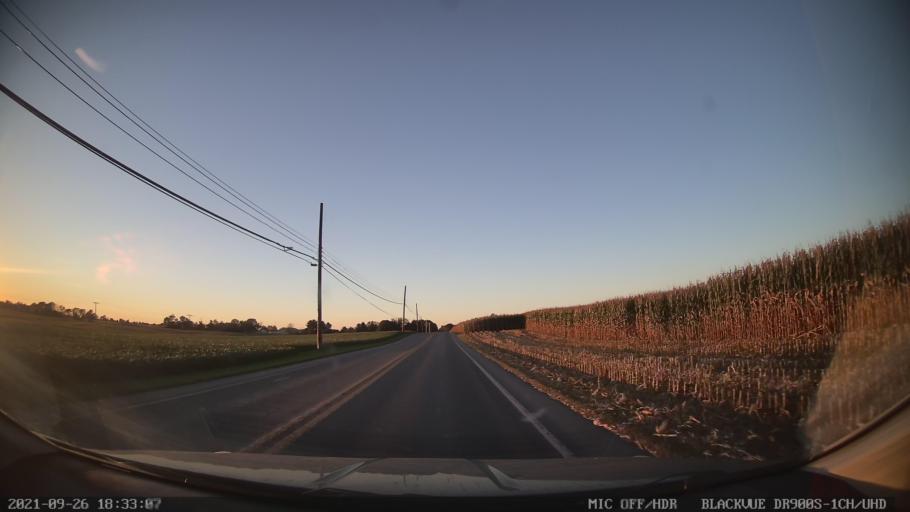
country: US
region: Pennsylvania
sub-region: Berks County
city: Kutztown
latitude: 40.4975
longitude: -75.7648
